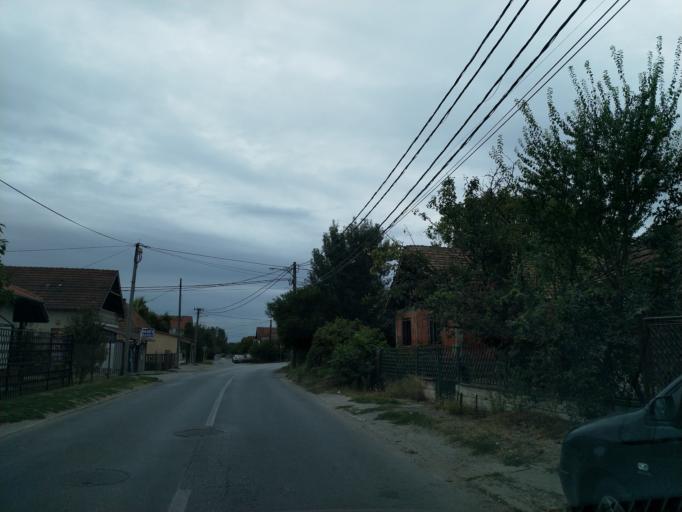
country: RS
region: Central Serbia
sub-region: Pomoravski Okrug
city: Paracin
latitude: 43.8554
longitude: 21.3975
